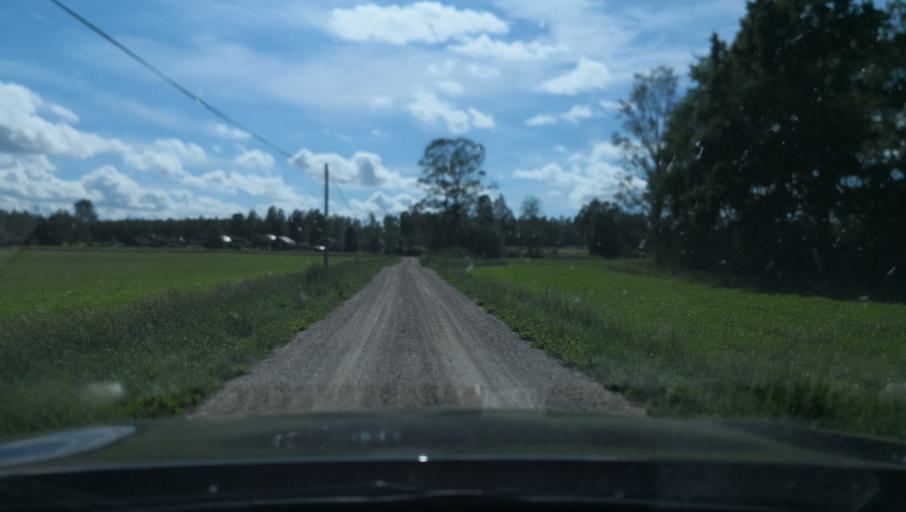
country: SE
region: Vaestmanland
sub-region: Kungsors Kommun
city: Kungsoer
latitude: 59.3200
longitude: 16.0550
